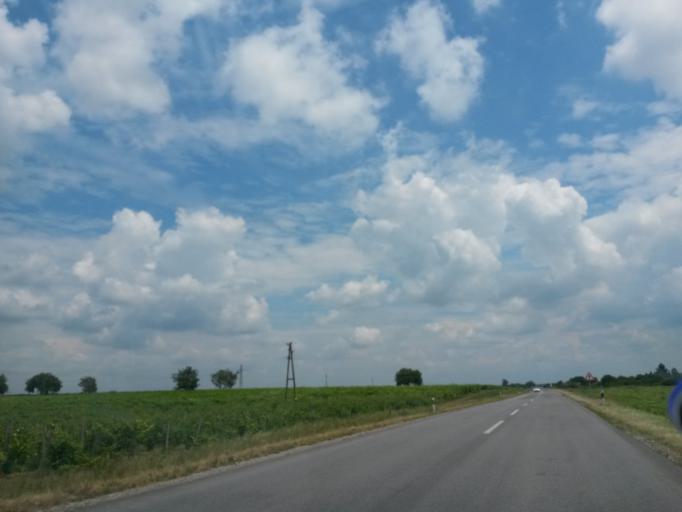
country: HR
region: Osjecko-Baranjska
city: Dalj
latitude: 45.5048
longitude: 19.0102
